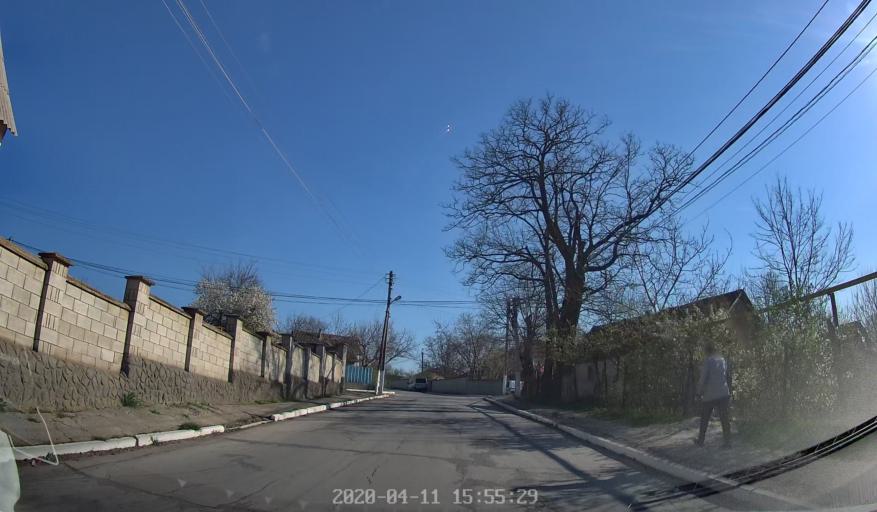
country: MD
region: Chisinau
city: Vadul lui Voda
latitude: 47.0957
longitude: 29.1772
